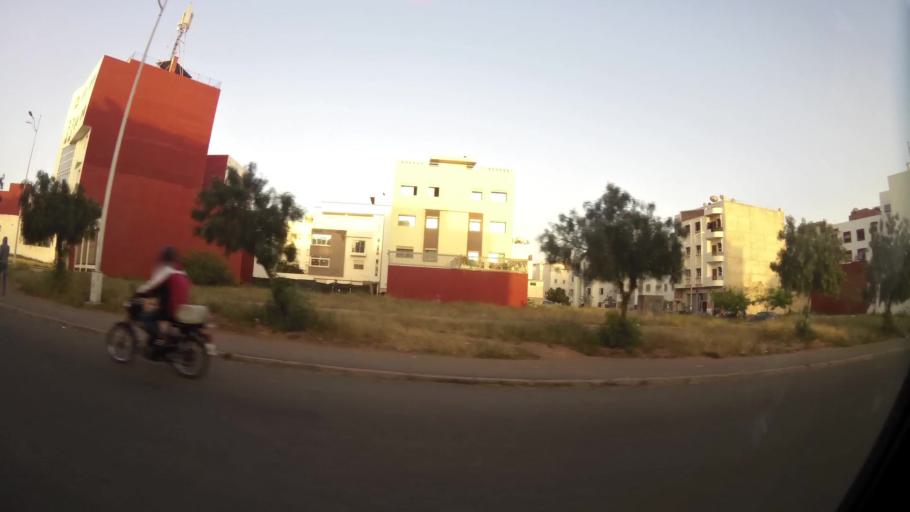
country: MA
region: Oued ed Dahab-Lagouira
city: Dakhla
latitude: 30.3923
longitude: -9.5657
